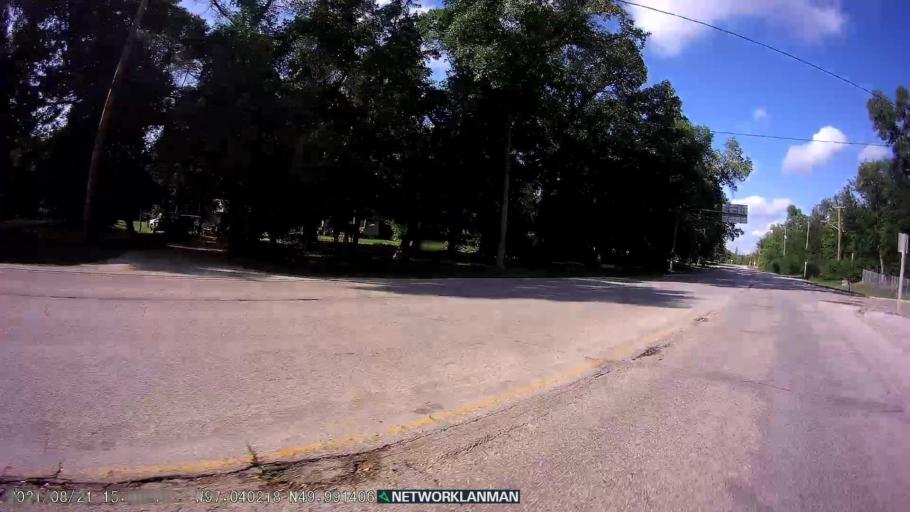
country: CA
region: Manitoba
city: Winnipeg
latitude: 49.9916
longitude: -97.0400
